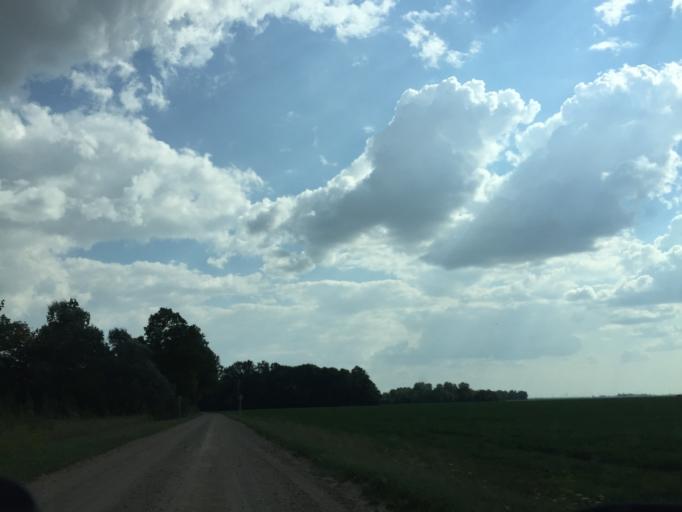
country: LV
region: Jelgava
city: Jelgava
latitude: 56.5095
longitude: 23.7548
